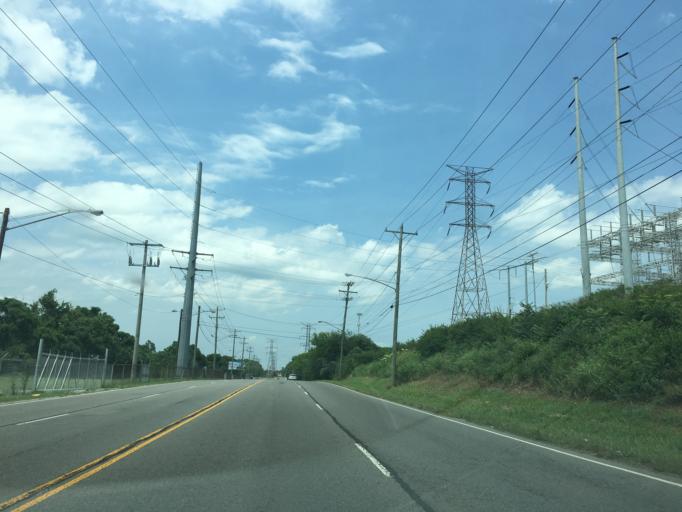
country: US
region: Tennessee
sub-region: Davidson County
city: Nashville
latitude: 36.1297
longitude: -86.7601
